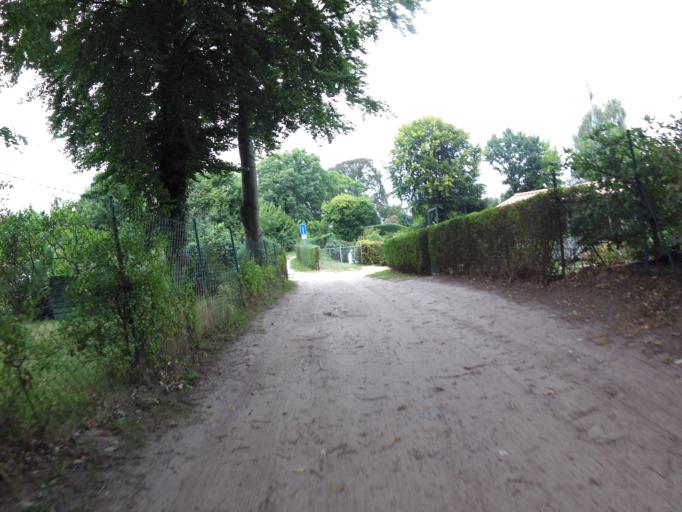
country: DE
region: Mecklenburg-Vorpommern
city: Seebad Heringsdorf
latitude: 53.9347
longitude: 14.1870
